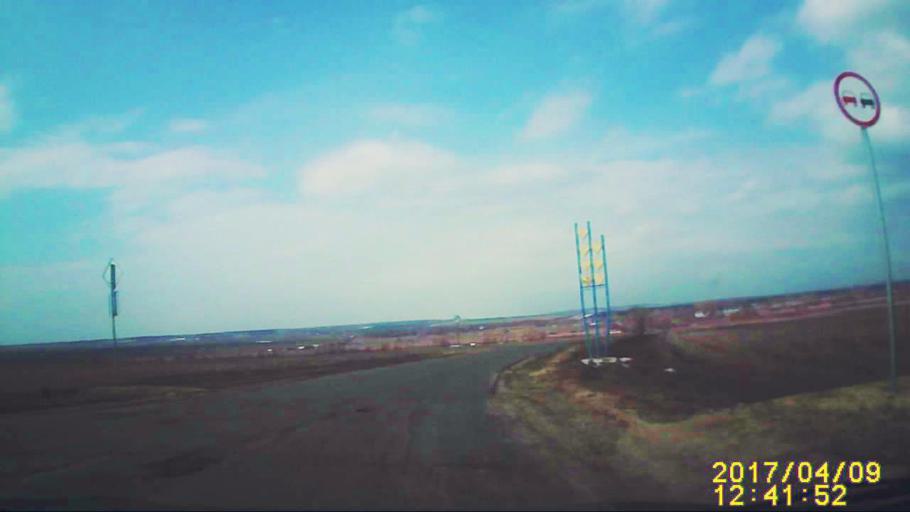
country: RU
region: Ulyanovsk
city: Ignatovka
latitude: 54.0007
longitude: 47.9315
